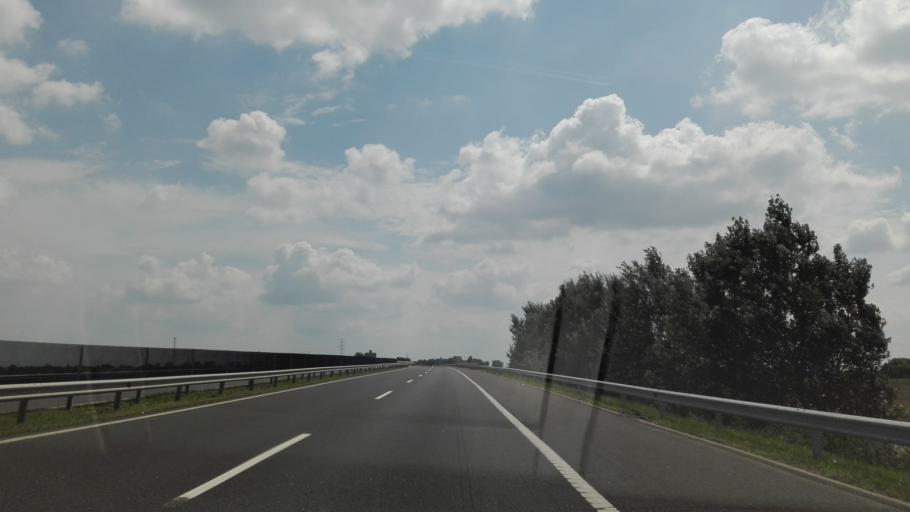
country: HU
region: Fejer
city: dunaujvaros
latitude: 46.9844
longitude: 18.8847
